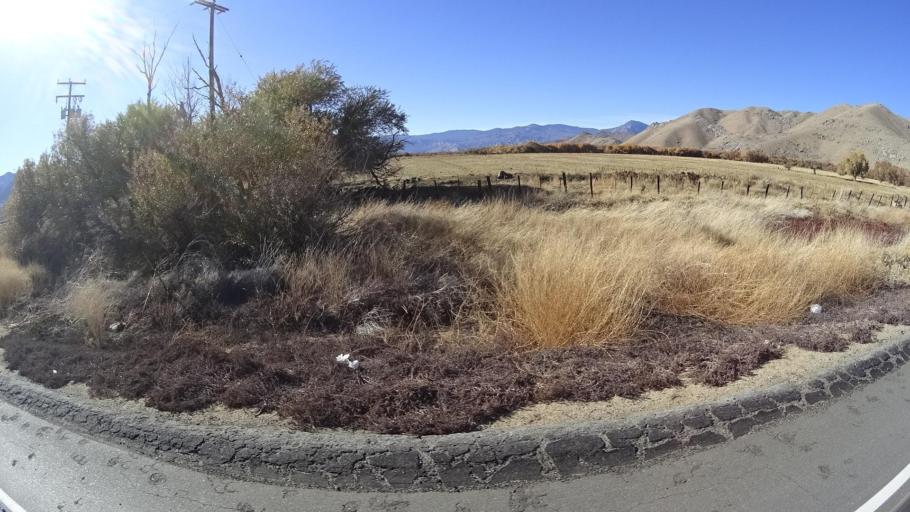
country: US
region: California
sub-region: Kern County
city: Weldon
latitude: 35.6623
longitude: -118.3225
